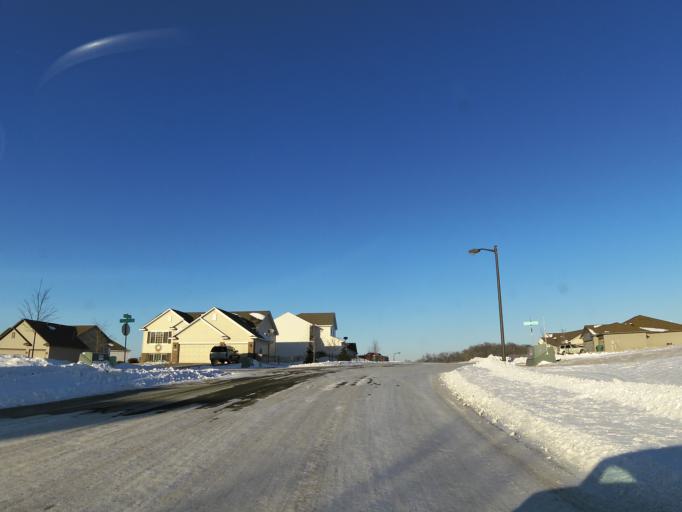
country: US
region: Minnesota
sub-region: Rice County
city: Lonsdale
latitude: 44.4868
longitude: -93.4175
